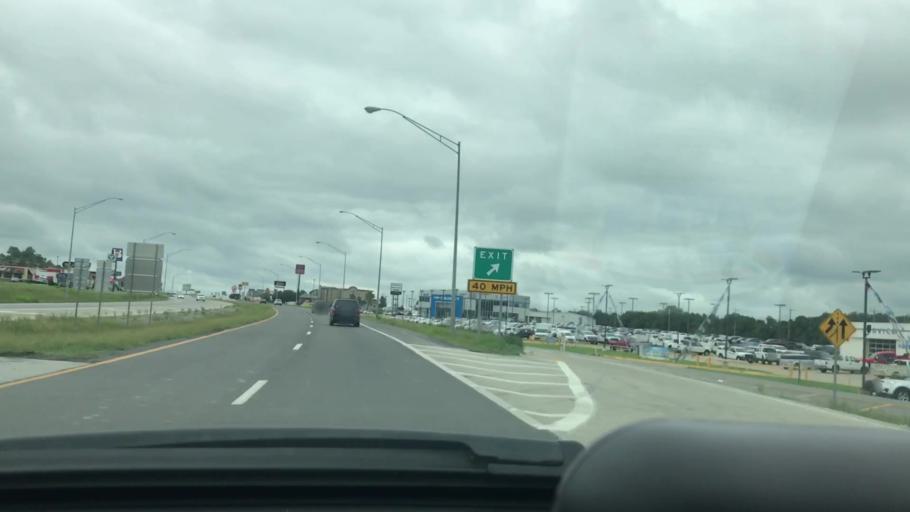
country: US
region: Oklahoma
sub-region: Pittsburg County
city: McAlester
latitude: 34.9091
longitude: -95.7454
